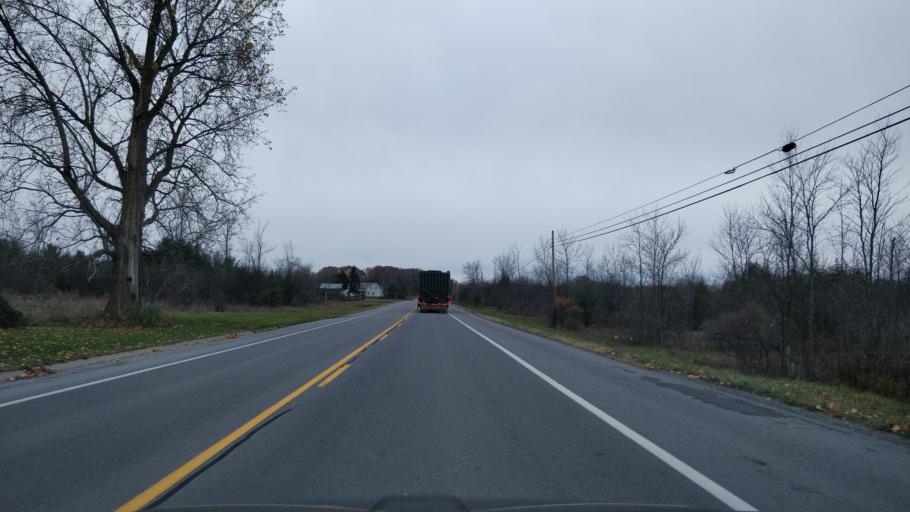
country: CA
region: Ontario
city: Brockville
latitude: 44.6179
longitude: -75.5956
